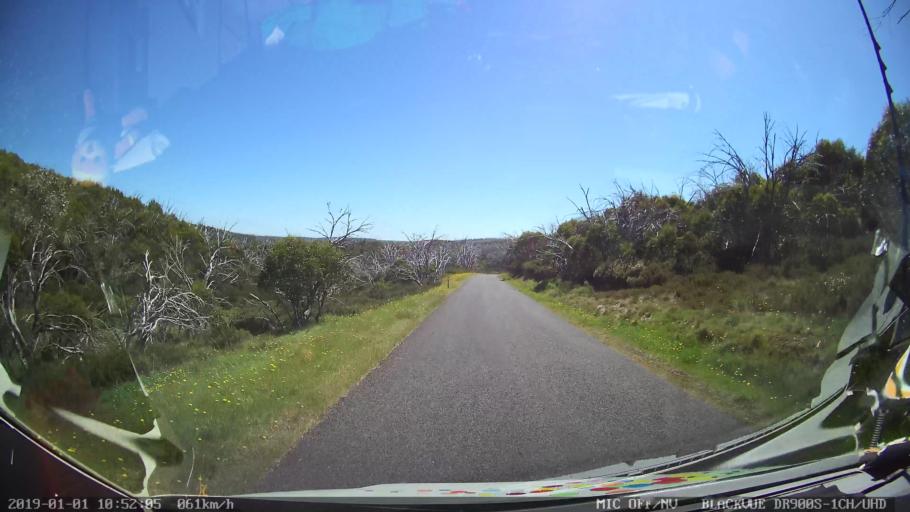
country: AU
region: New South Wales
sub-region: Snowy River
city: Jindabyne
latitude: -36.0179
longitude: 148.3772
